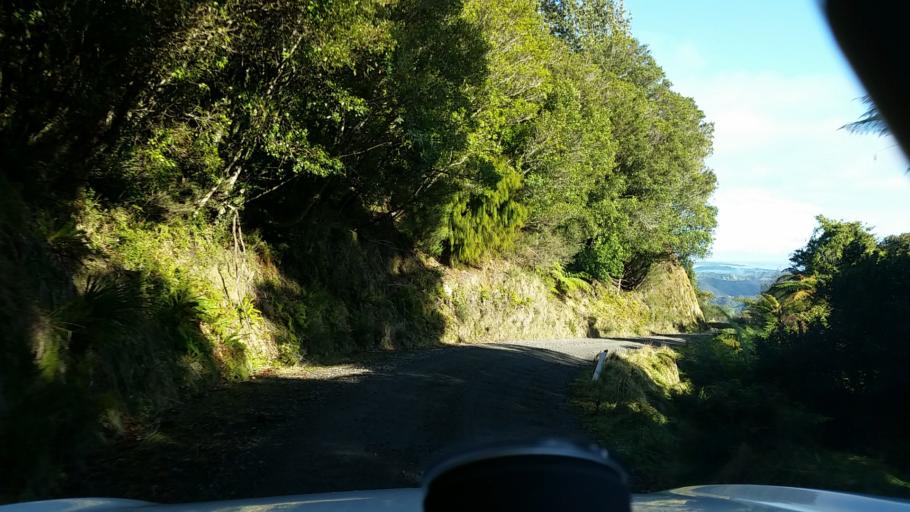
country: NZ
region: Taranaki
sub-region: South Taranaki District
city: Eltham
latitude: -39.4031
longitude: 174.5629
